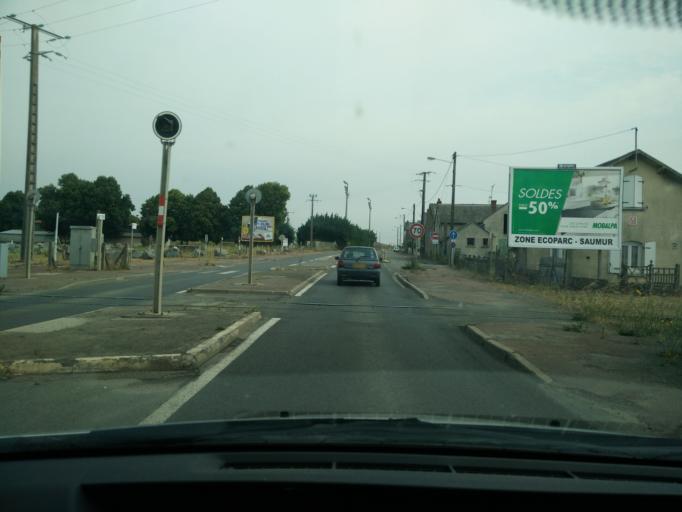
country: FR
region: Poitou-Charentes
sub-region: Departement des Deux-Sevres
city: Thouars
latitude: 46.9836
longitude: -0.1987
